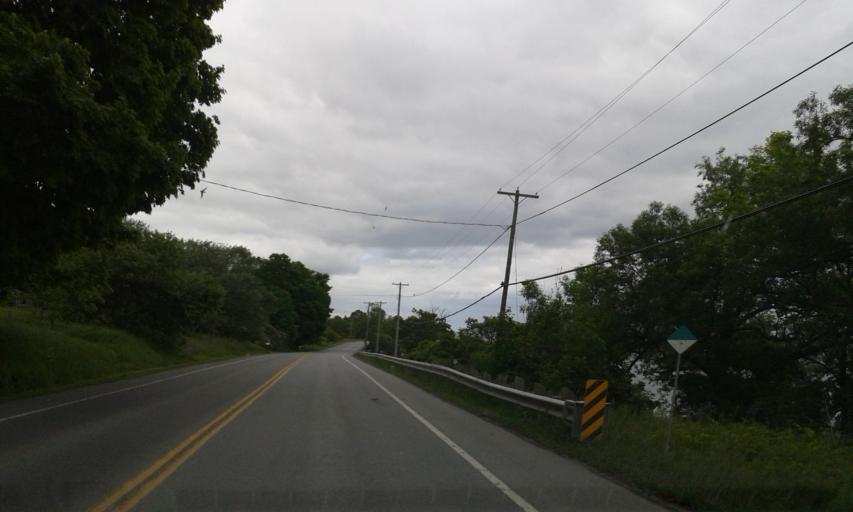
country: CA
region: Ontario
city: Skatepark
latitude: 44.1559
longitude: -76.8221
